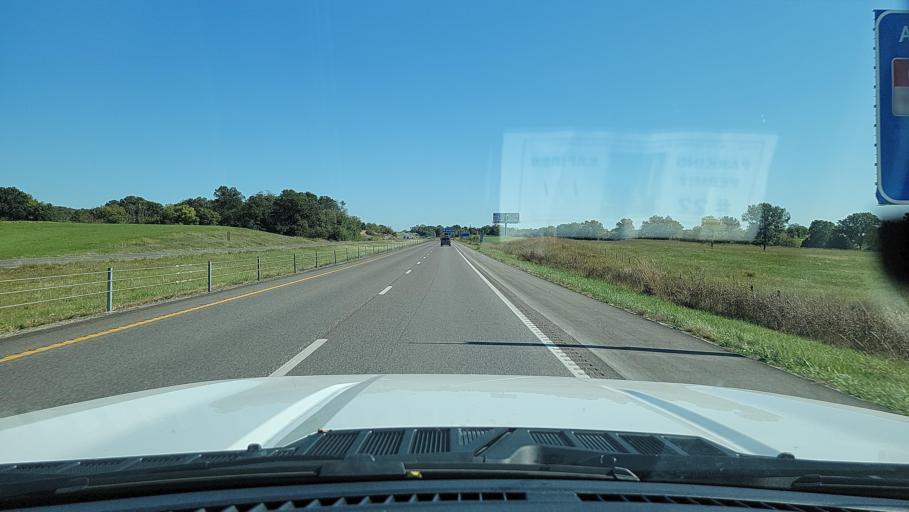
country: US
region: Missouri
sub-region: Sainte Genevieve County
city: Sainte Genevieve
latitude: 37.9488
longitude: -90.1461
